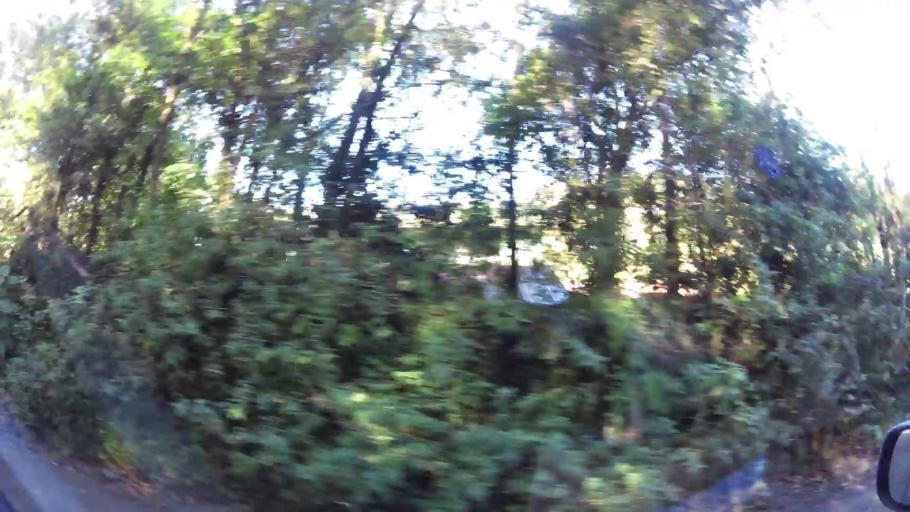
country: CR
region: Guanacaste
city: Juntas
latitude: 10.3067
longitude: -84.8117
